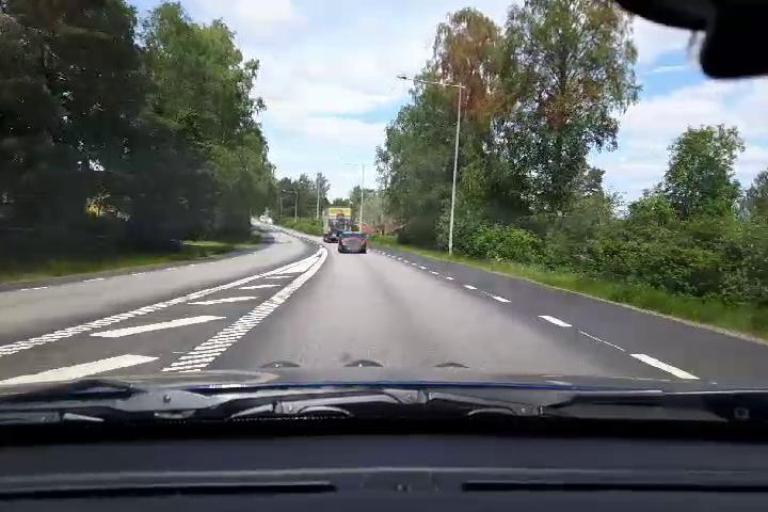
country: SE
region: Uppsala
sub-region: Osthammars Kommun
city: Bjorklinge
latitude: 60.0334
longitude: 17.5523
